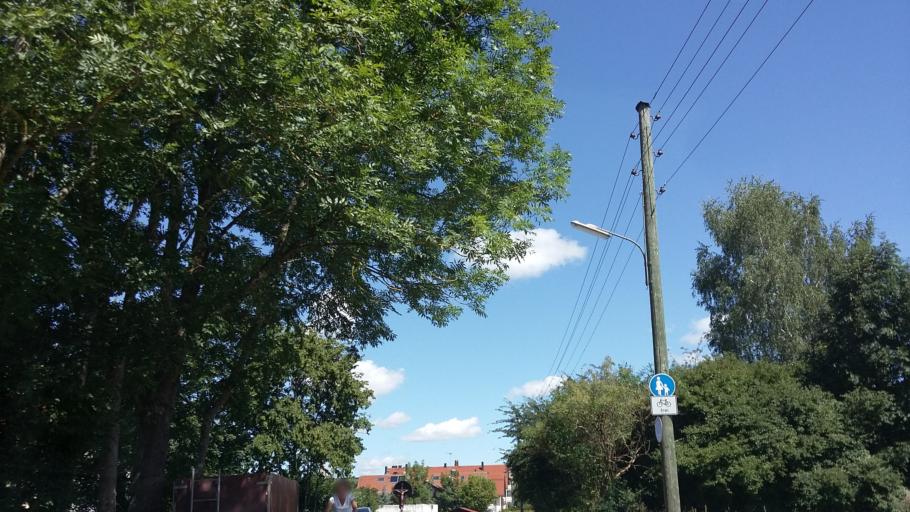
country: DE
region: Bavaria
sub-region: Upper Bavaria
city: Gauting
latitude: 48.0639
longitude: 11.3810
